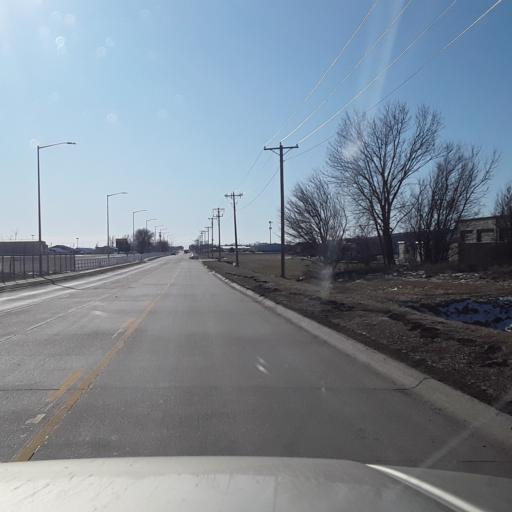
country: US
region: Nebraska
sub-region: Adams County
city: Hastings
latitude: 40.5752
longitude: -98.4021
